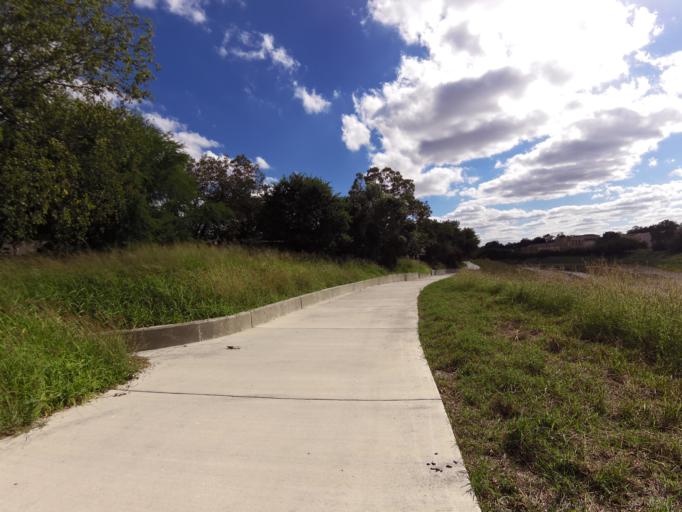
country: US
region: Texas
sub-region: Bexar County
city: San Antonio
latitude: 29.4027
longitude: -98.5064
